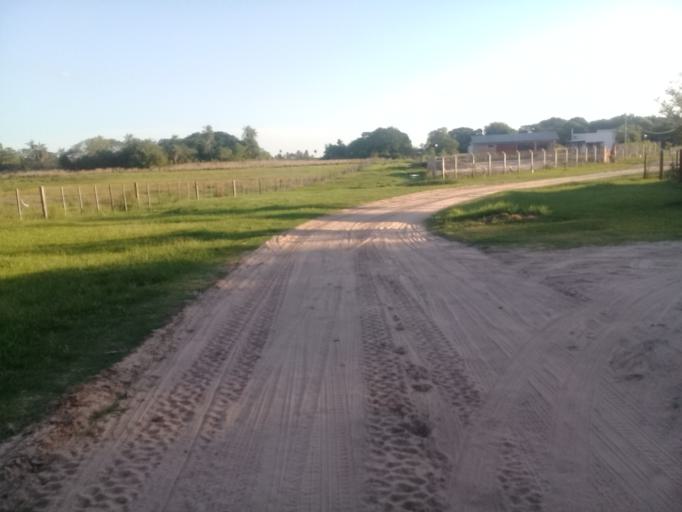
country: AR
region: Corrientes
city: San Luis del Palmar
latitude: -27.4666
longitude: -58.6623
